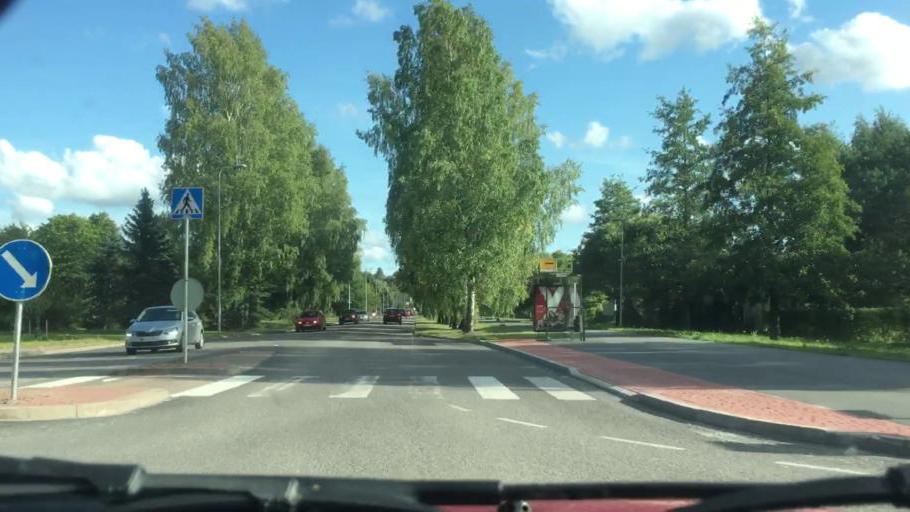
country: FI
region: Varsinais-Suomi
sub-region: Turku
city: Turku
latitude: 60.4642
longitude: 22.2413
